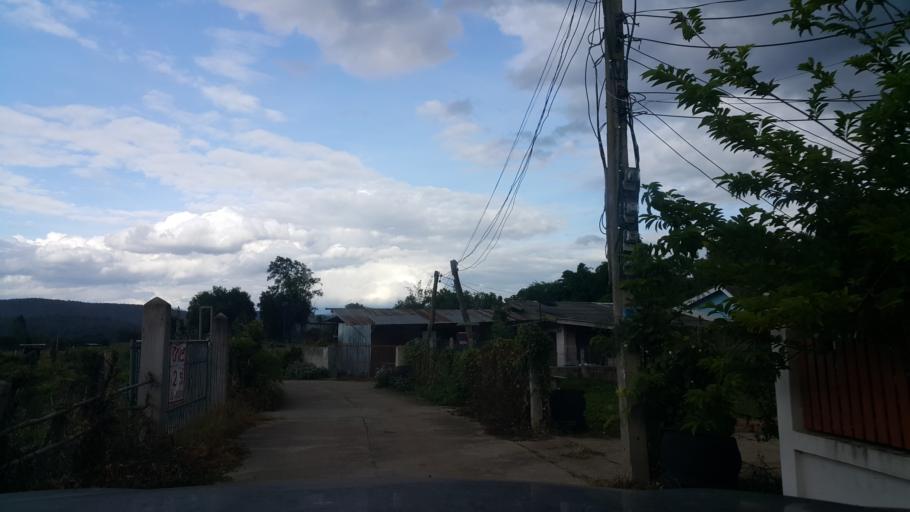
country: TH
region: Chiang Mai
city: Mae Taeng
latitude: 19.0810
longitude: 98.9383
